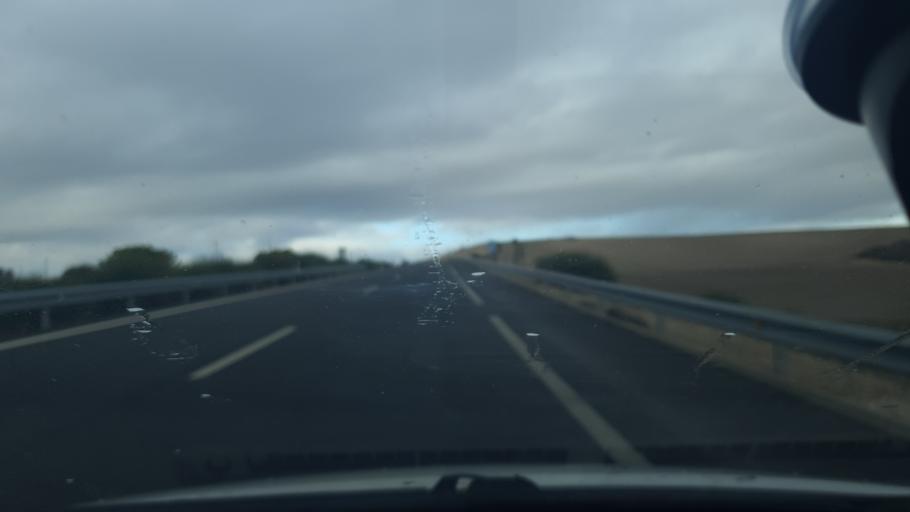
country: ES
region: Castille and Leon
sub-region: Provincia de Segovia
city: Cuellar
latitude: 41.3998
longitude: -4.2932
